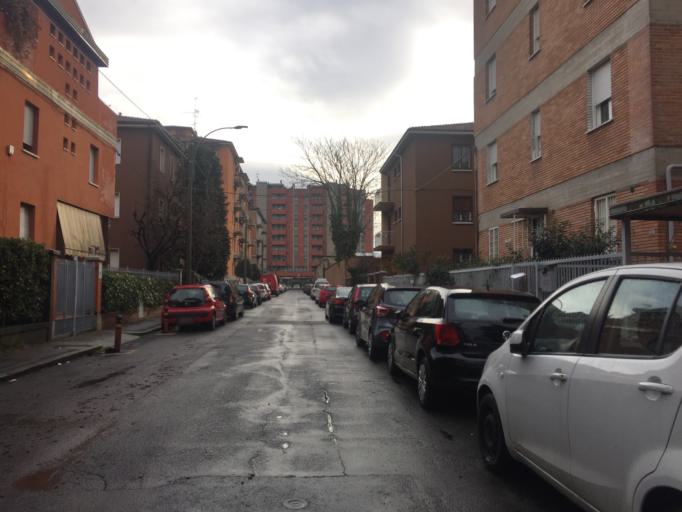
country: IT
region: Emilia-Romagna
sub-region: Provincia di Bologna
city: Casalecchio di Reno
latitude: 44.5049
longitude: 11.2930
